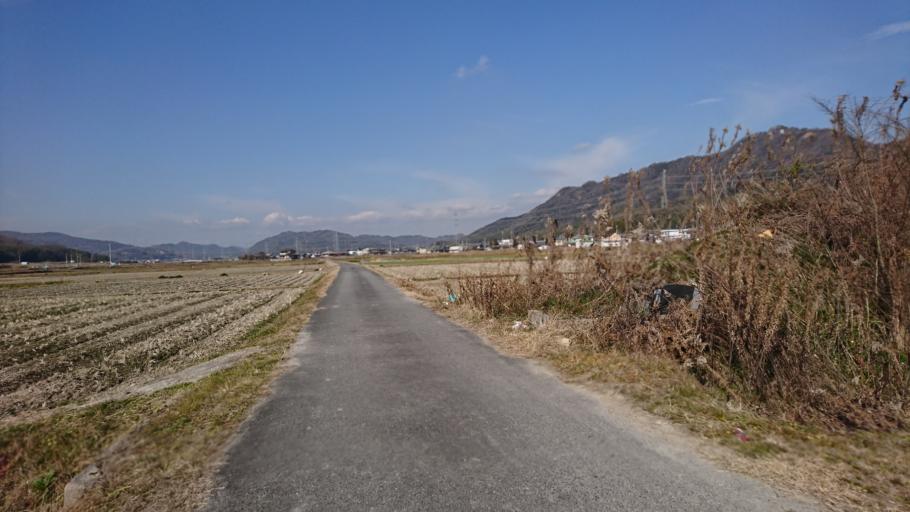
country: JP
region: Hyogo
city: Kakogawacho-honmachi
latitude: 34.8164
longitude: 134.8529
